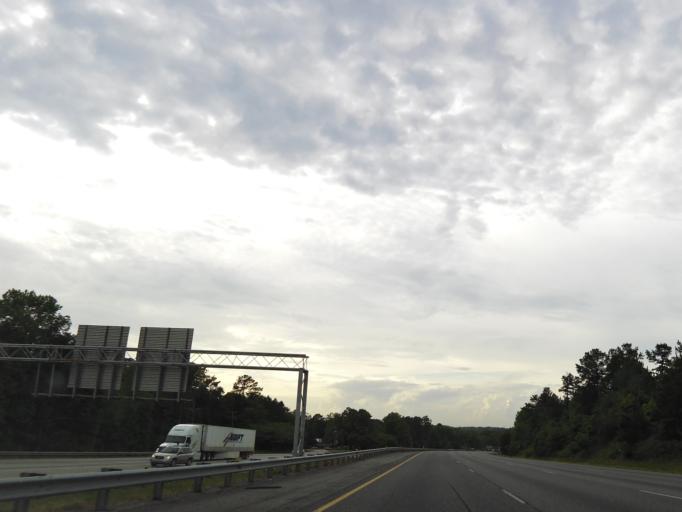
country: US
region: Georgia
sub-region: Monroe County
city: Forsyth
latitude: 32.9701
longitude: -83.8247
